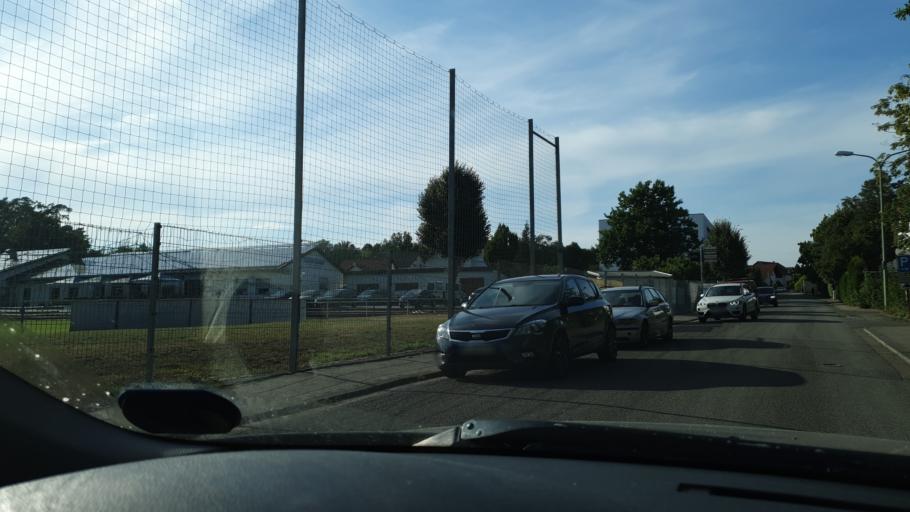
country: DE
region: Rheinland-Pfalz
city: Rodenbach
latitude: 49.4703
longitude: 7.6426
